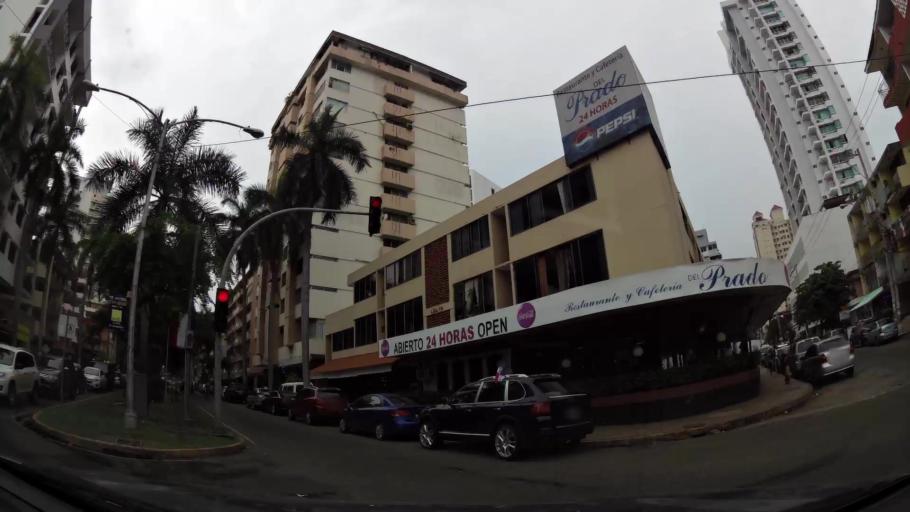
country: PA
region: Panama
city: Panama
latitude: 8.9884
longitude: -79.5245
